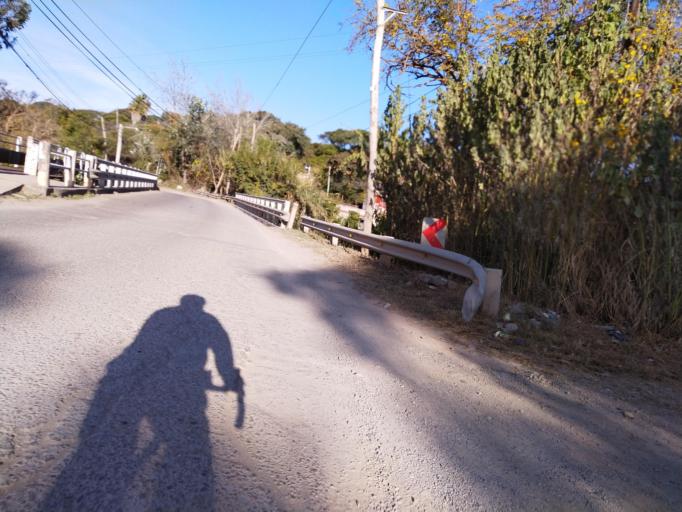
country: AR
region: Jujuy
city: San Salvador de Jujuy
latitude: -24.1796
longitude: -65.3428
